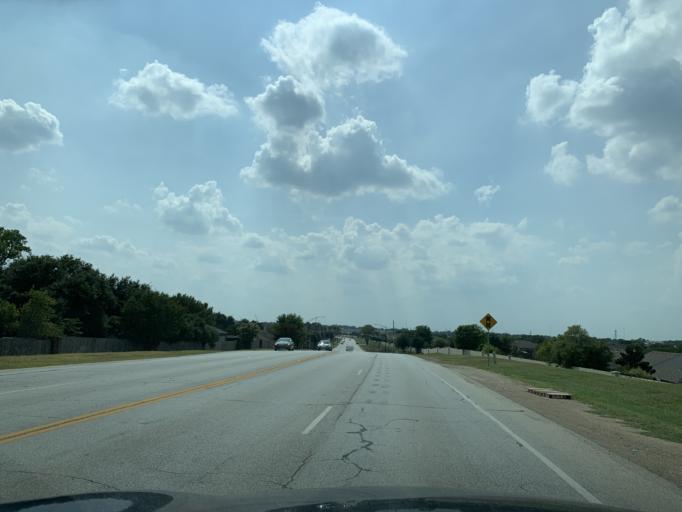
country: US
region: Texas
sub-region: Tarrant County
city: Hurst
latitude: 32.8027
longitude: -97.1929
